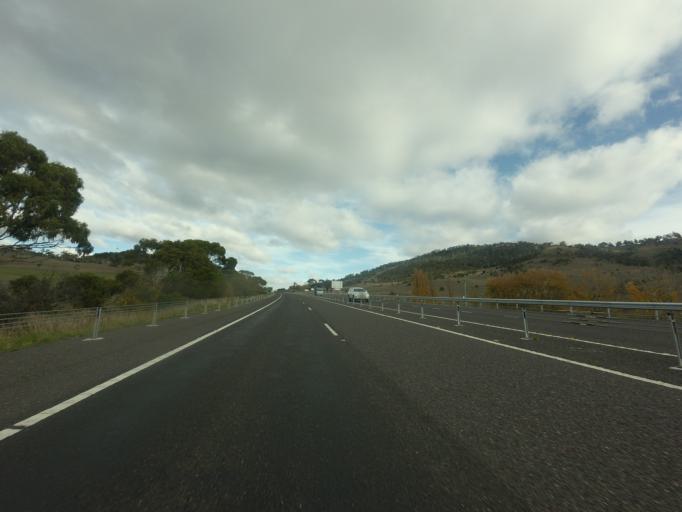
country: AU
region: Tasmania
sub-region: Brighton
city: Bridgewater
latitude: -42.5426
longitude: 147.2063
